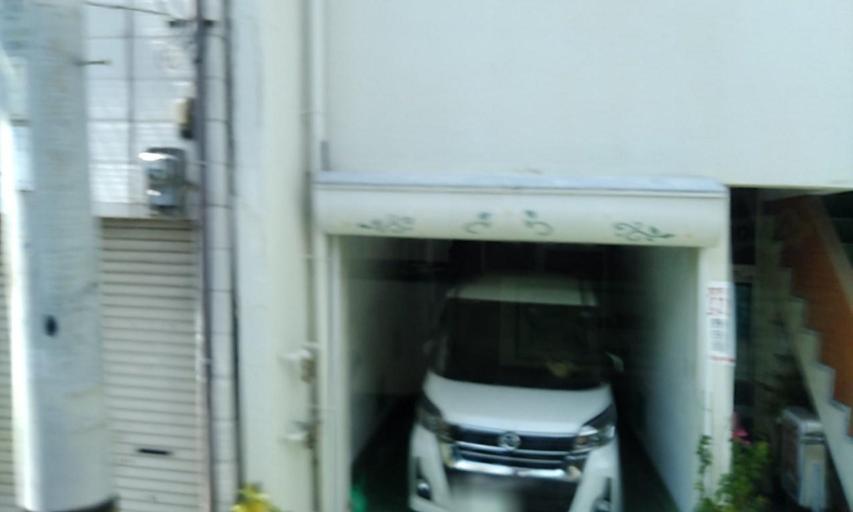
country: JP
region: Kagawa
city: Takamatsu-shi
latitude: 34.3374
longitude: 134.0520
